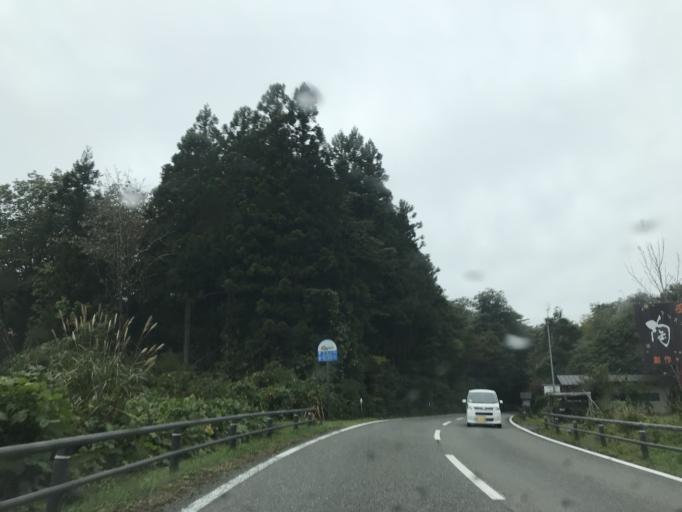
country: JP
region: Iwate
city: Ichinoseki
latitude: 38.9713
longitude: 140.9788
